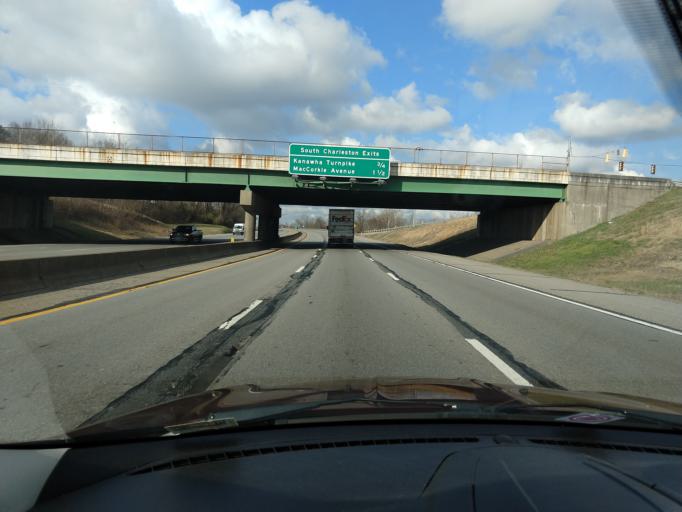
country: US
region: West Virginia
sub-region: Kanawha County
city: South Charleston
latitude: 38.3640
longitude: -81.6859
